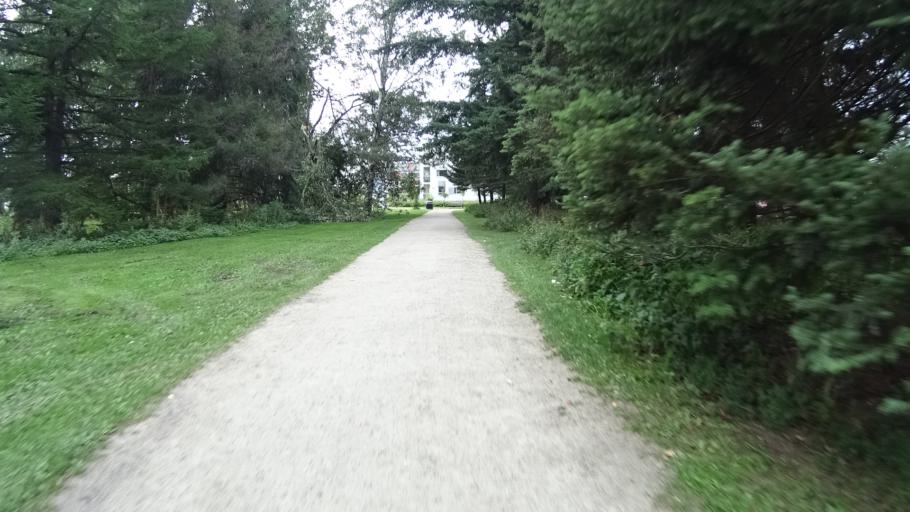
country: FI
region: Uusimaa
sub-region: Helsinki
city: Teekkarikylae
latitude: 60.2370
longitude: 24.8540
